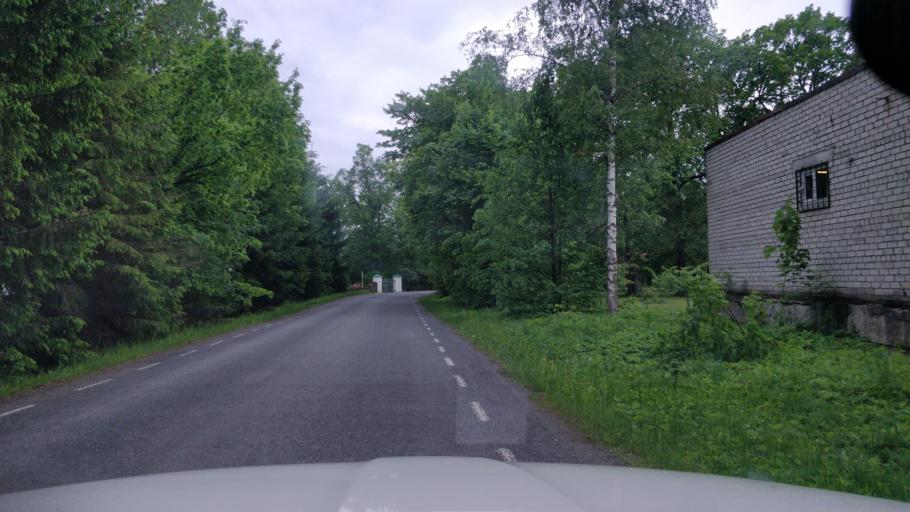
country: EE
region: Paernumaa
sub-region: Halinga vald
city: Parnu-Jaagupi
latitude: 58.7115
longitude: 24.3686
